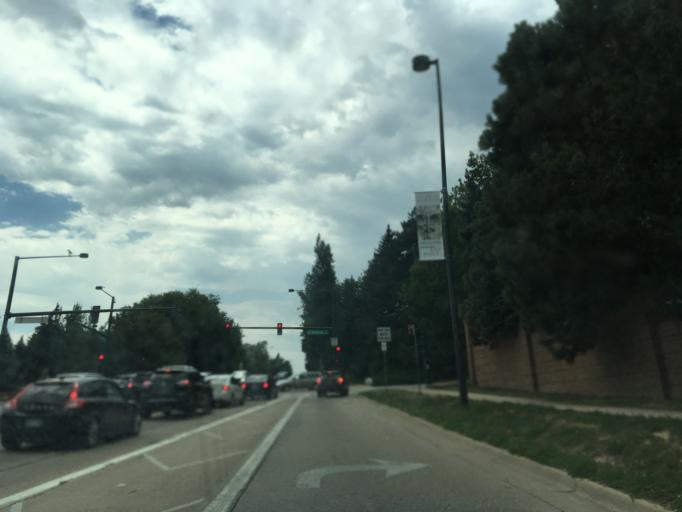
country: US
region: Colorado
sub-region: Arapahoe County
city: Glendale
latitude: 39.7117
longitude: -104.9594
